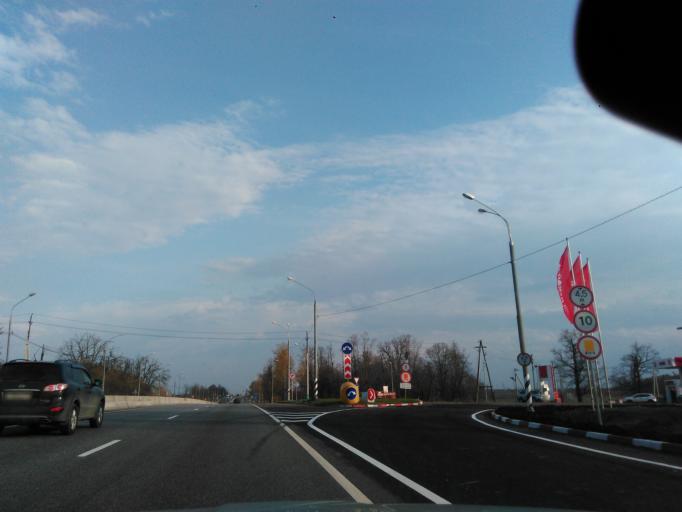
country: RU
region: Moskovskaya
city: Peshki
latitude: 56.1188
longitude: 37.0813
